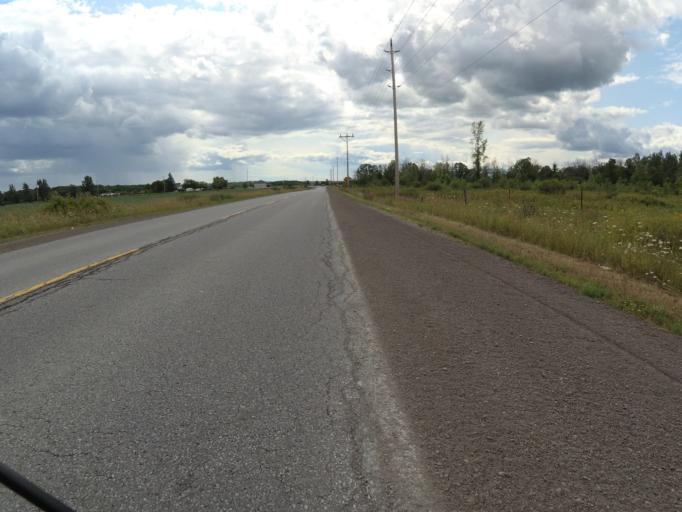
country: CA
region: Ontario
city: Bells Corners
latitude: 45.4490
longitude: -76.0359
